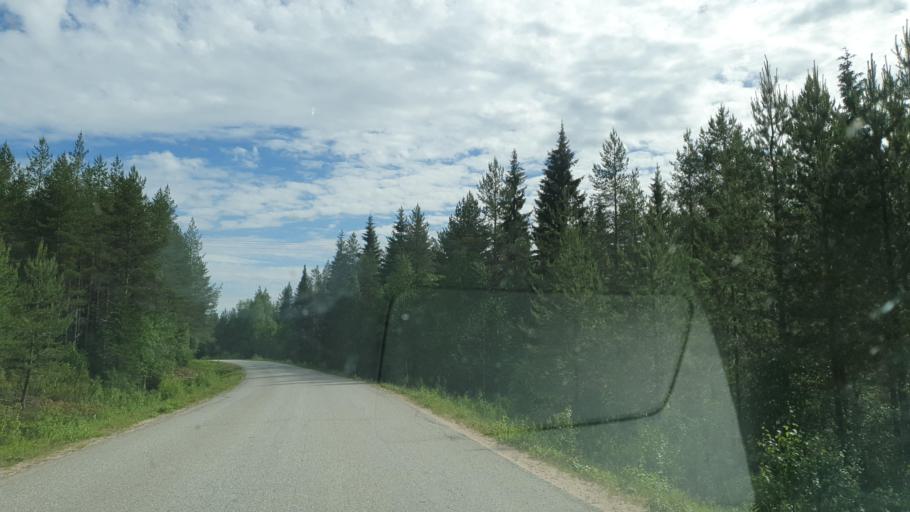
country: FI
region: Kainuu
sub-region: Kehys-Kainuu
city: Suomussalmi
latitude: 64.5941
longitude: 29.1002
